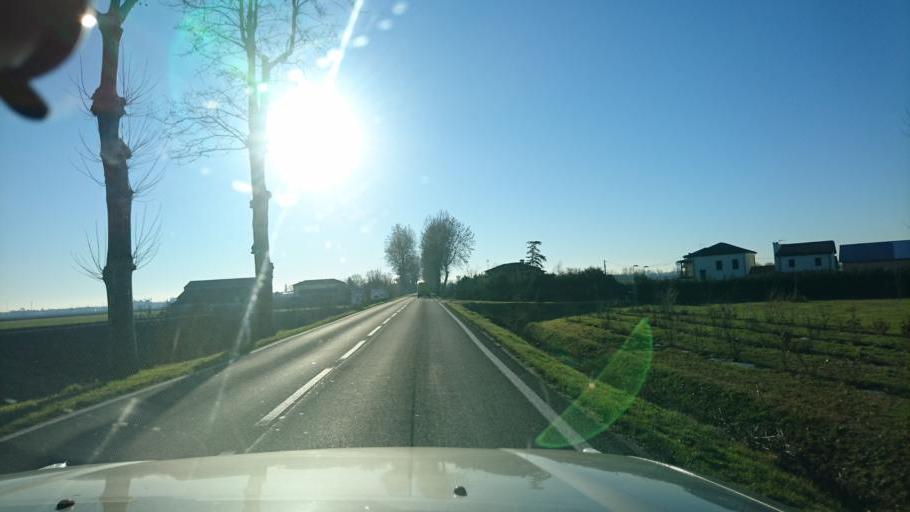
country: IT
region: Veneto
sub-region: Provincia di Venezia
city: Cavarzere
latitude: 45.1512
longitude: 12.0598
